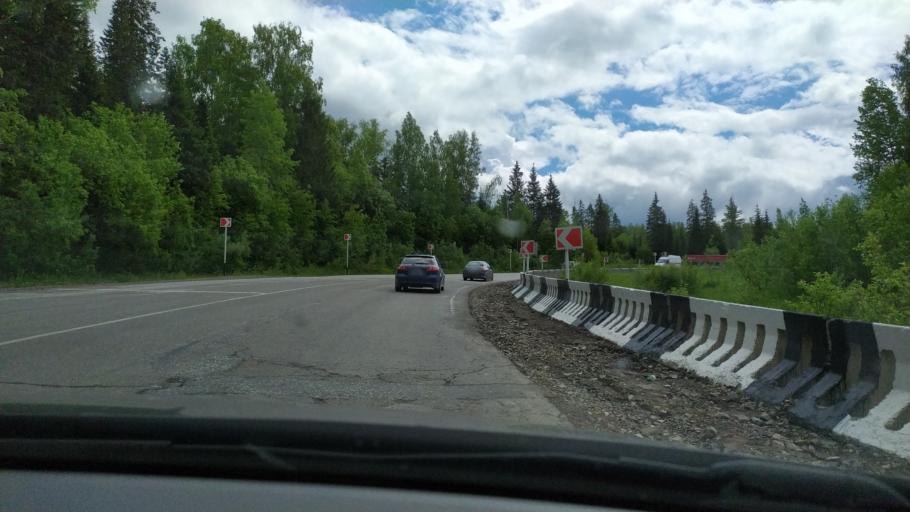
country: RU
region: Perm
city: Gremyachinsk
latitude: 58.4413
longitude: 57.8871
